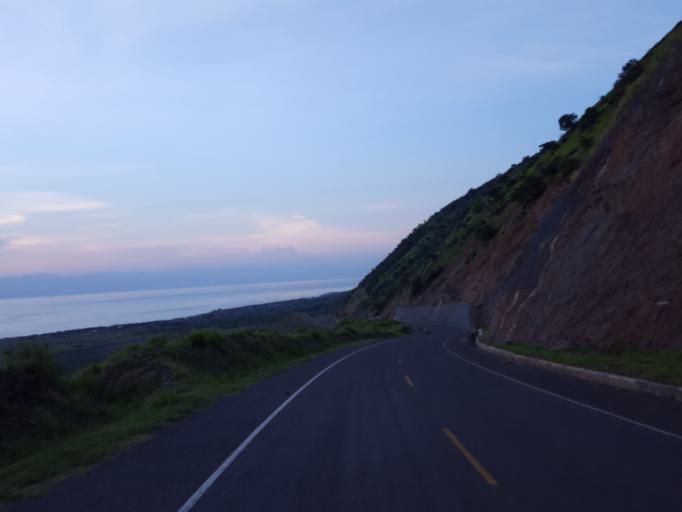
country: UG
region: Western Region
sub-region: Kibale District
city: Kagadi
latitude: 1.2427
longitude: 30.7582
